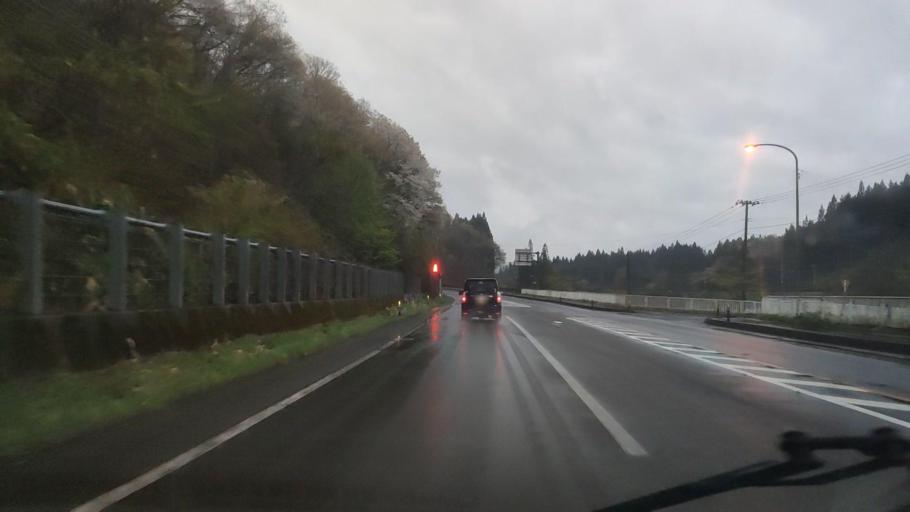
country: JP
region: Akita
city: Omagari
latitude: 39.5713
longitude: 140.3230
